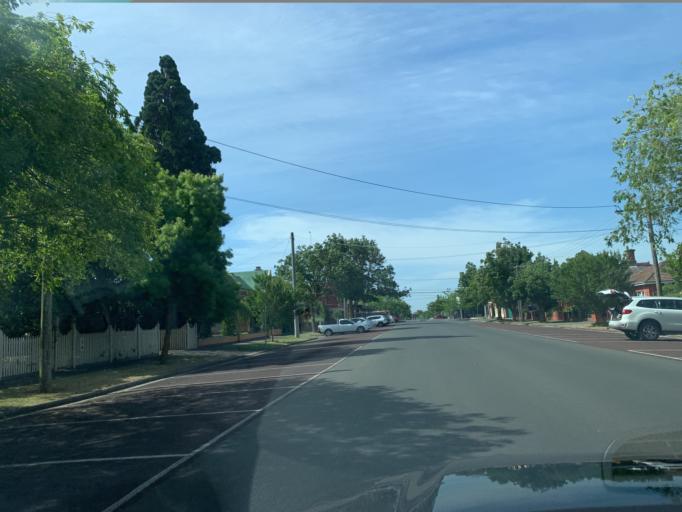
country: AU
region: Victoria
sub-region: Ballarat North
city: Ballarat Central
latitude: -37.5626
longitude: 143.8501
